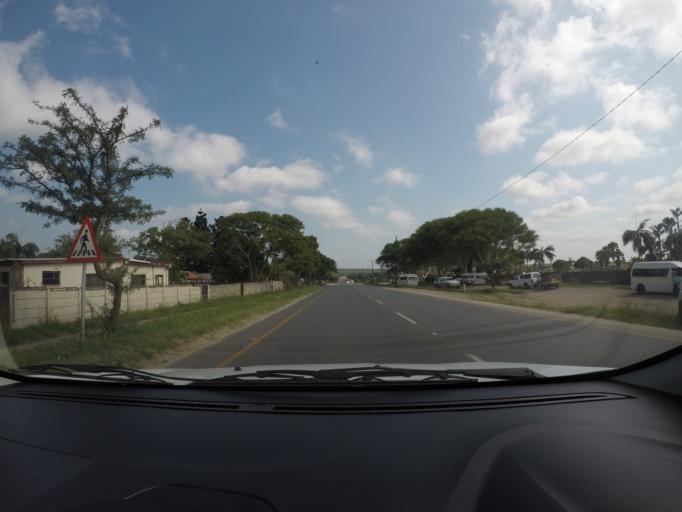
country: ZA
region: KwaZulu-Natal
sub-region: uThungulu District Municipality
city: eSikhawini
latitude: -28.8805
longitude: 31.9028
